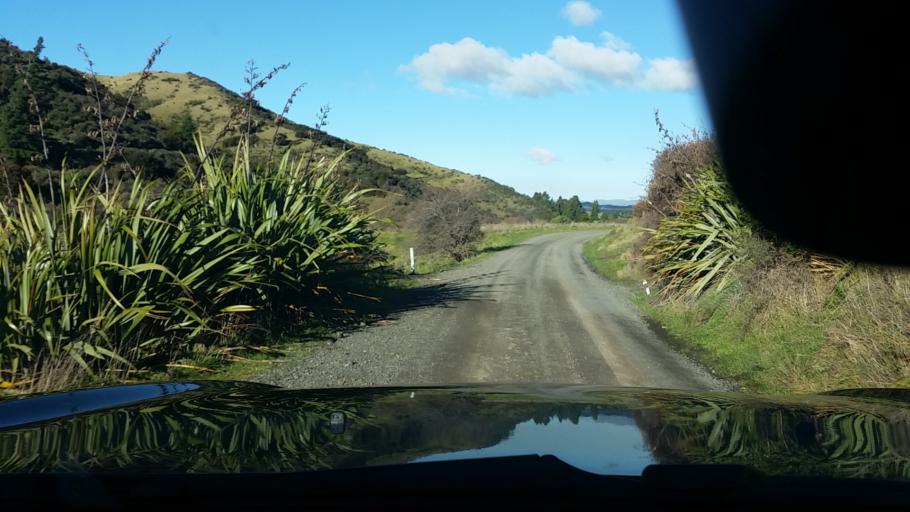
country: NZ
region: Marlborough
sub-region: Marlborough District
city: Blenheim
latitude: -41.6511
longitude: 173.9712
